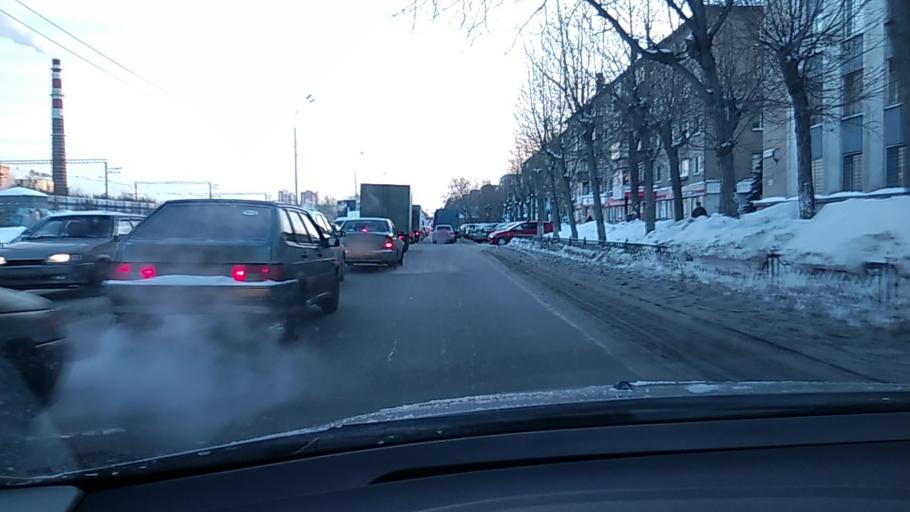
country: RU
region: Sverdlovsk
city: Yekaterinburg
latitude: 56.8404
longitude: 60.6324
